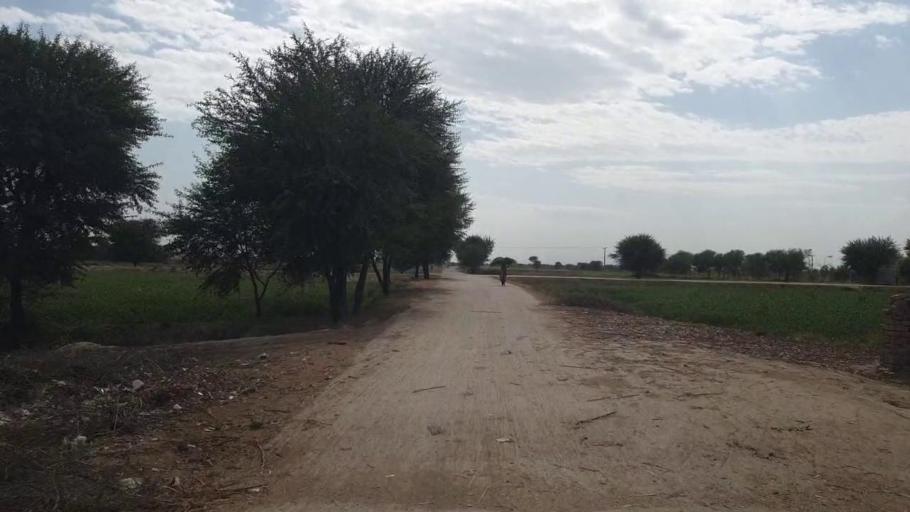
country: PK
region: Sindh
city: Hala
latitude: 25.9368
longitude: 68.4288
